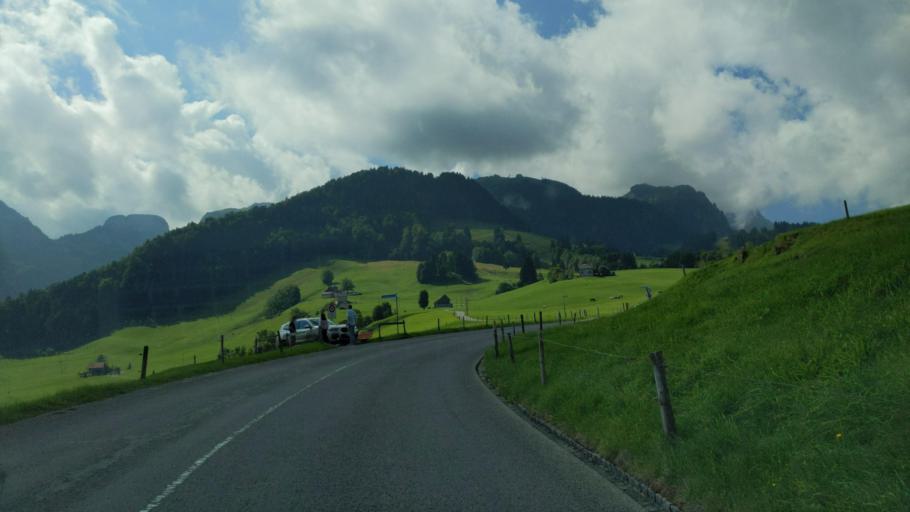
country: CH
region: Appenzell Innerrhoden
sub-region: Appenzell Inner Rhodes
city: Appenzell
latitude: 47.3051
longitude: 9.4307
